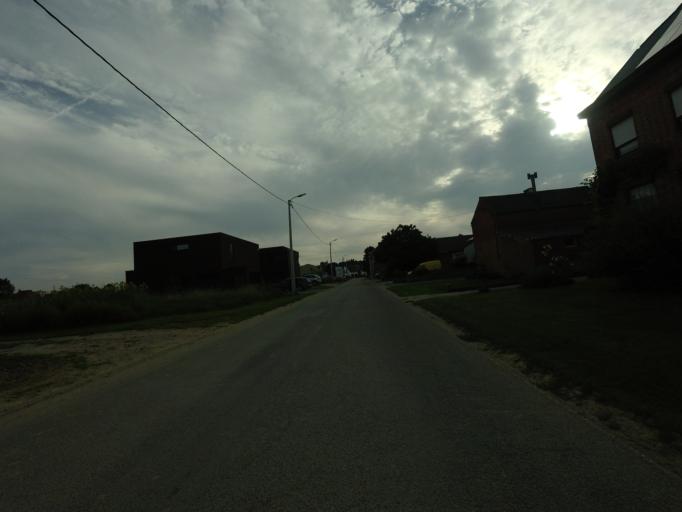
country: BE
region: Flanders
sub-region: Provincie Vlaams-Brabant
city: Boortmeerbeek
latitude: 50.9748
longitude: 4.5814
